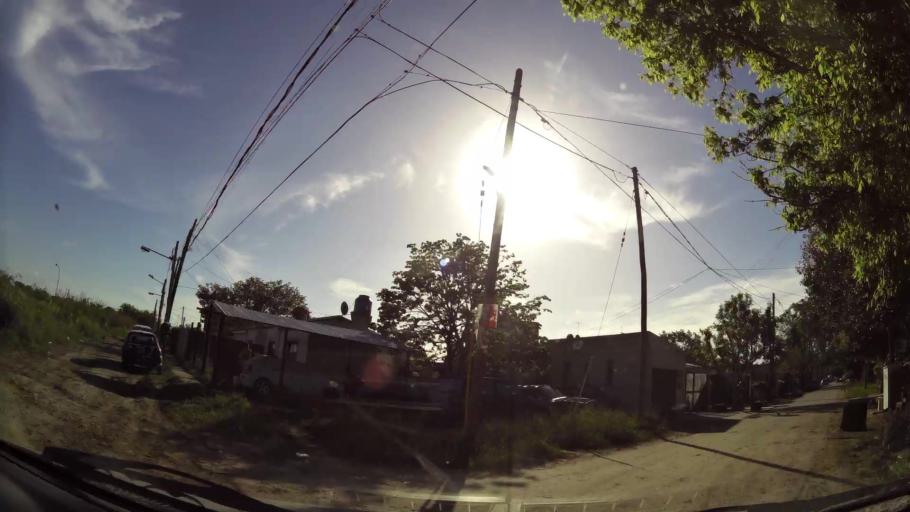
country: AR
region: Buenos Aires
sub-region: Partido de Quilmes
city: Quilmes
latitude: -34.7945
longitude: -58.2176
